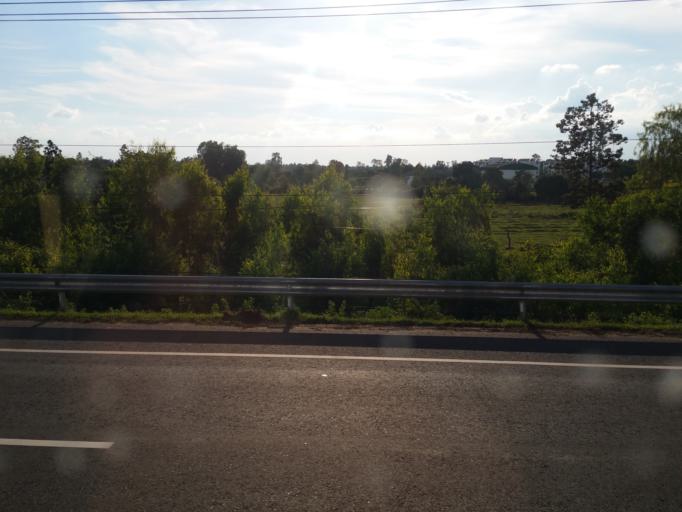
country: TH
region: Changwat Ubon Ratchathani
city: Sirindhorn
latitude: 15.1910
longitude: 105.3677
